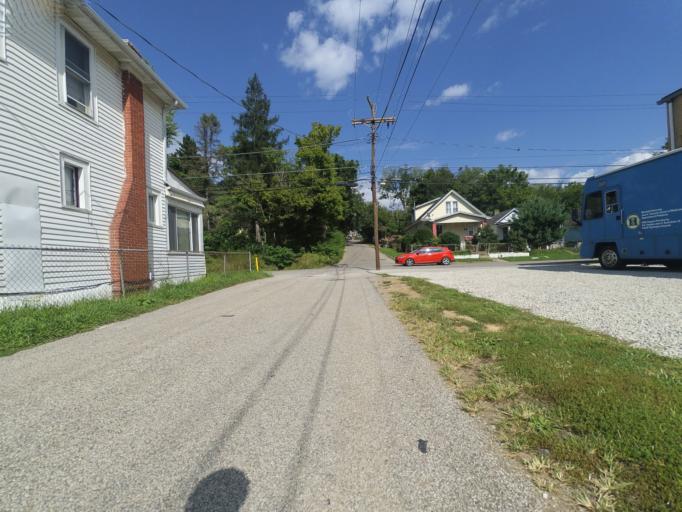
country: US
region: West Virginia
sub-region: Cabell County
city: Huntington
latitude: 38.4097
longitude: -82.4234
